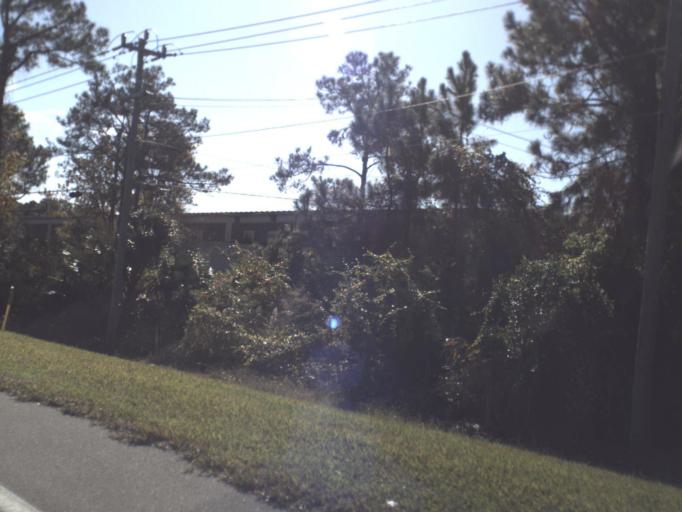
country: US
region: Florida
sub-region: Volusia County
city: Holly Hill
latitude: 29.2153
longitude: -81.0788
